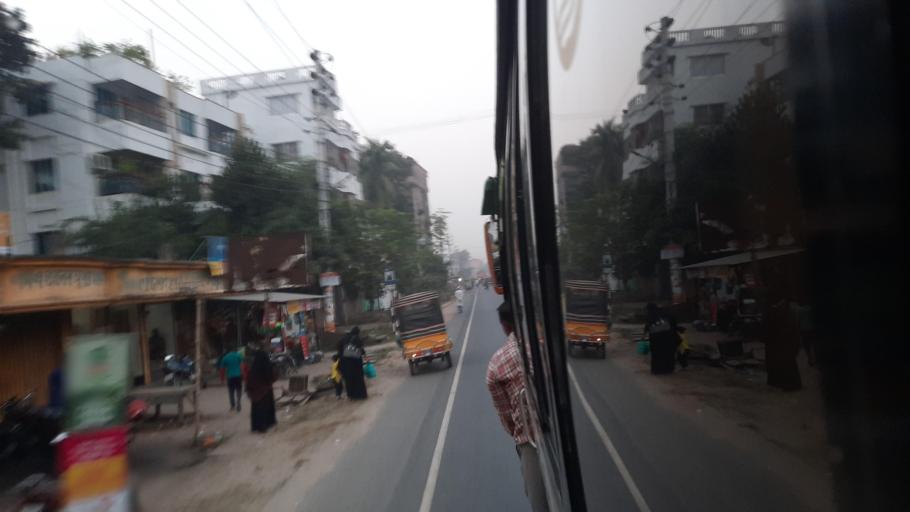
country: BD
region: Khulna
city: Jessore
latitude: 23.1758
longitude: 89.1919
